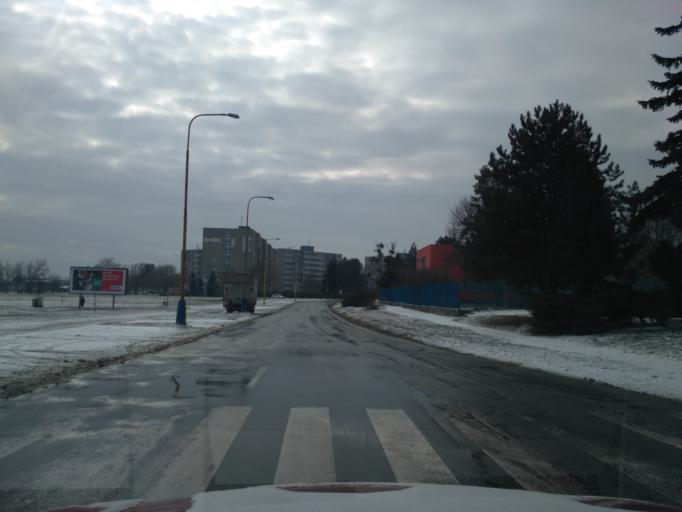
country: SK
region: Kosicky
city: Kosice
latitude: 48.7008
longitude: 21.2340
